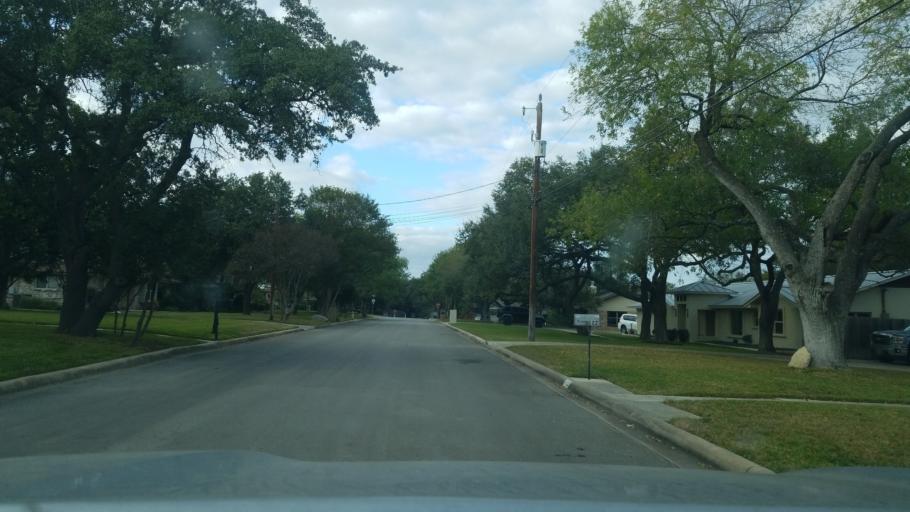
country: US
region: Texas
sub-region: Bexar County
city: Hollywood Park
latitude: 29.6026
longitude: -98.4841
